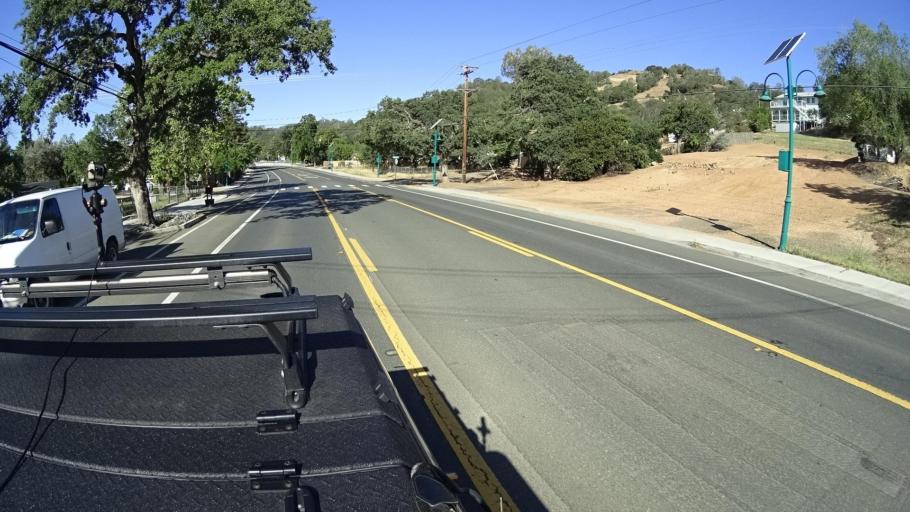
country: US
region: California
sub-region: Lake County
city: Clearlake Oaks
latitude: 39.0267
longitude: -122.6703
